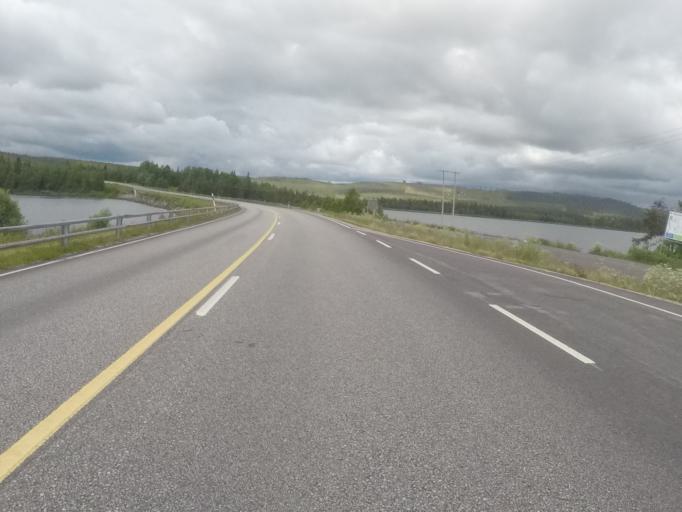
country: FI
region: Lapland
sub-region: Tunturi-Lappi
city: Muonio
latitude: 68.0311
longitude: 23.5587
